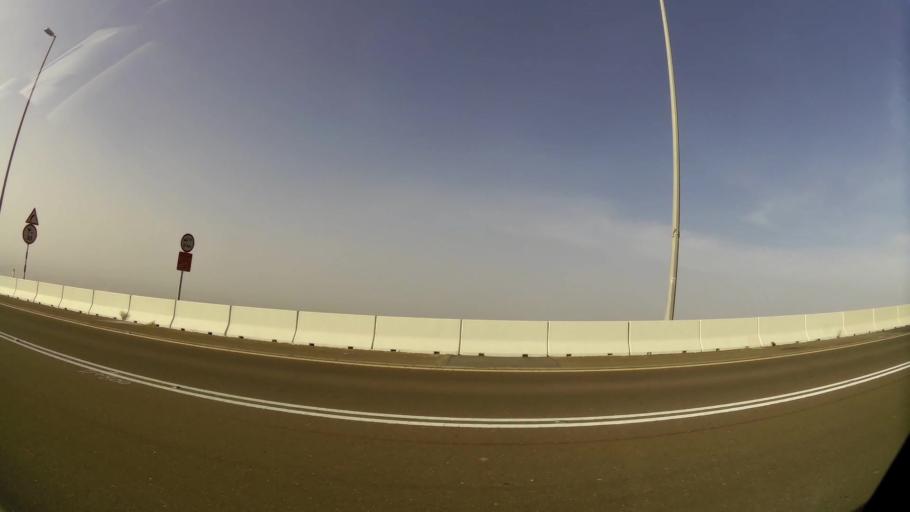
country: AE
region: Abu Dhabi
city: Al Ain
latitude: 24.0795
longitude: 55.7702
